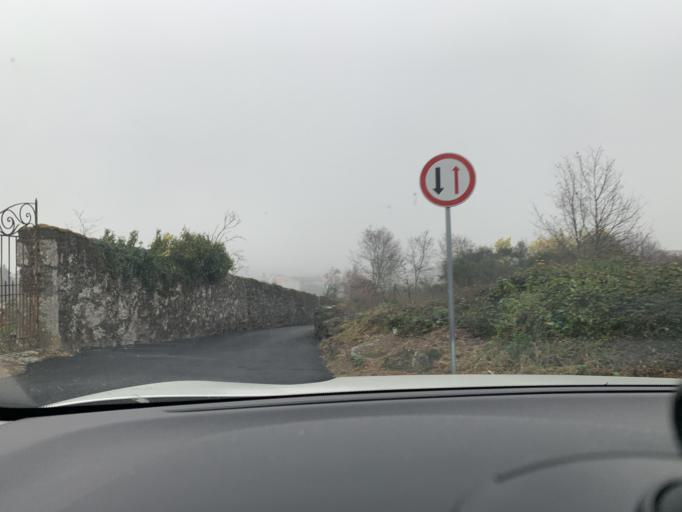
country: PT
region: Viseu
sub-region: Viseu
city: Viseu
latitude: 40.6587
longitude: -7.8959
